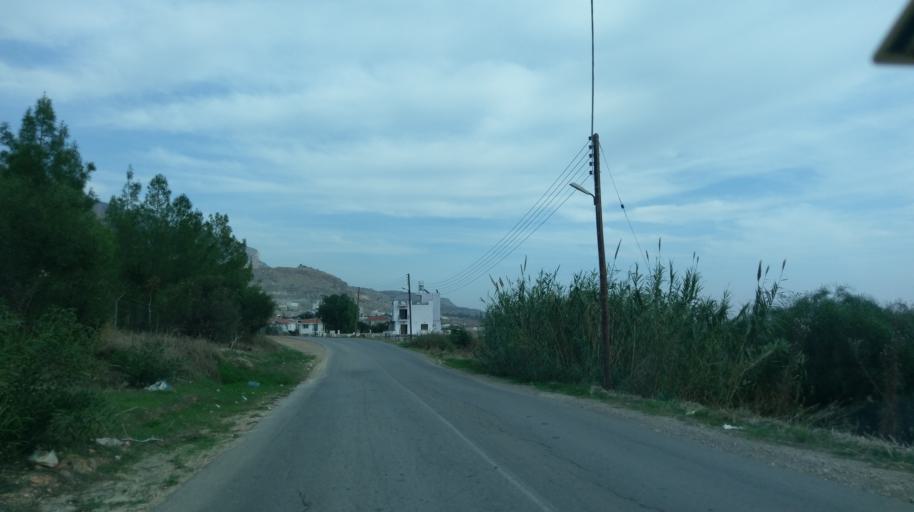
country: CY
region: Keryneia
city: Kyrenia
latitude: 35.2894
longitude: 33.2841
